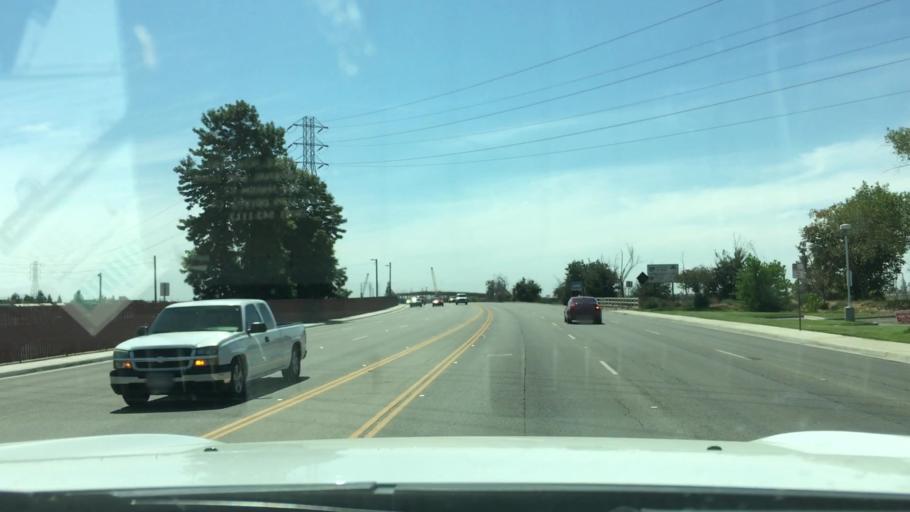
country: US
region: California
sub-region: Kern County
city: Bakersfield
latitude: 35.3730
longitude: -119.0493
